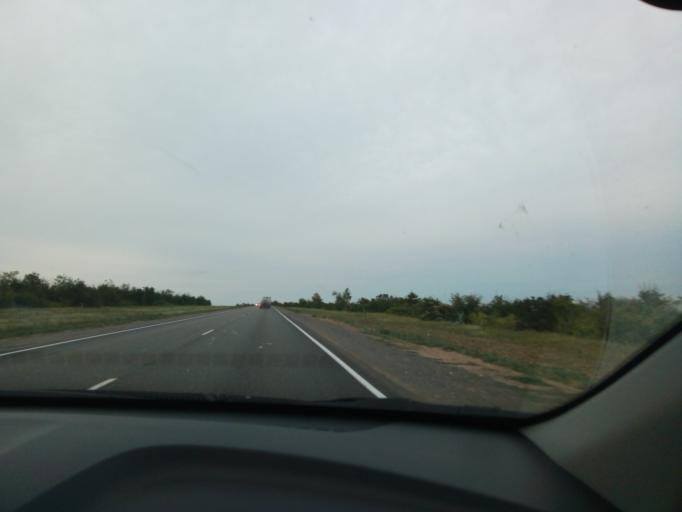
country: RU
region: Volgograd
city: Primorsk
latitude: 49.2067
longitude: 44.8993
